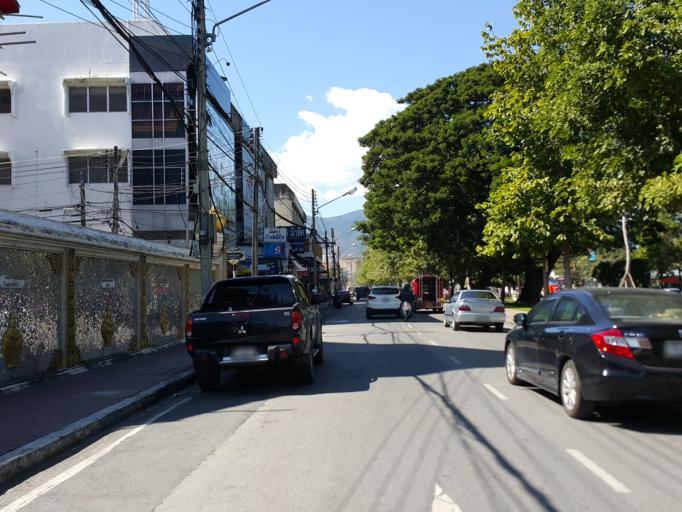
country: TH
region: Chiang Mai
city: Chiang Mai
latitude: 18.7953
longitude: 98.9854
